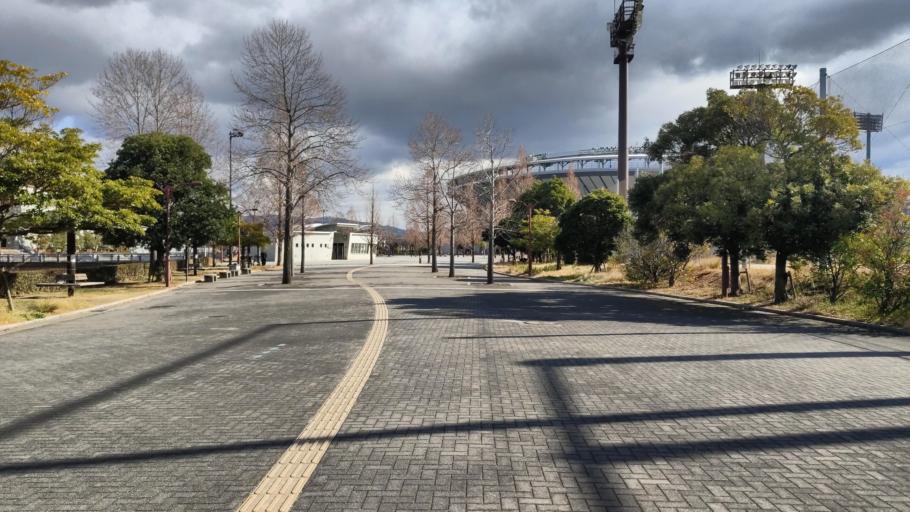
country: JP
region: Ehime
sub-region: Shikoku-chuo Shi
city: Matsuyama
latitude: 33.8093
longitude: 132.7441
